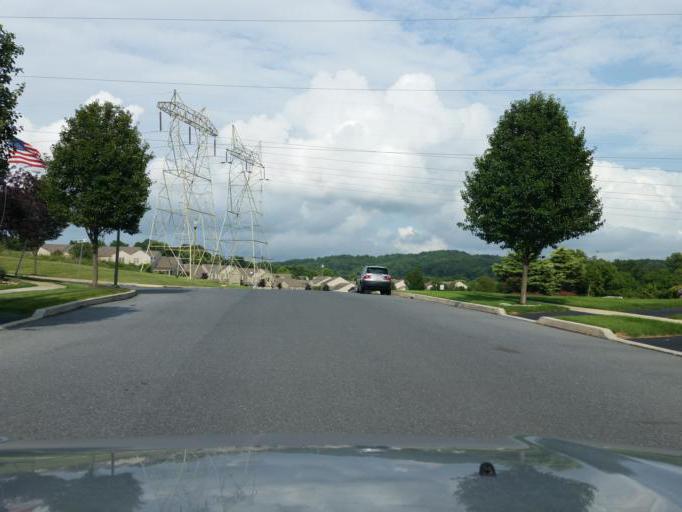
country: US
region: Pennsylvania
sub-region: Dauphin County
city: Hummelstown
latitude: 40.2464
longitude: -76.7159
